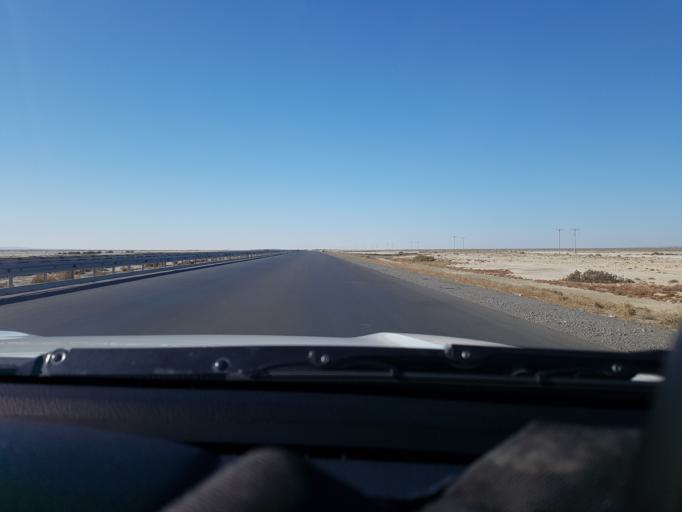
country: TM
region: Balkan
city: Gazanjyk
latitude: 39.2594
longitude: 55.1114
